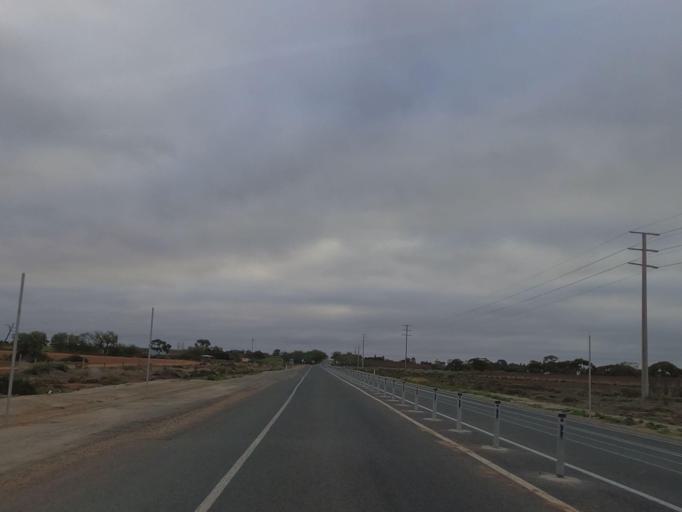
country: AU
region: Victoria
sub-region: Swan Hill
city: Swan Hill
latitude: -35.4710
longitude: 143.6666
